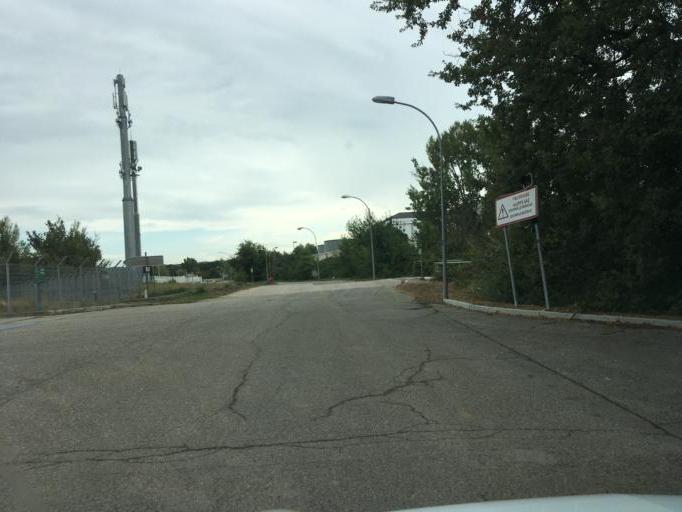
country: FR
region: Provence-Alpes-Cote d'Azur
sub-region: Departement des Bouches-du-Rhone
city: Rousset
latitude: 43.4740
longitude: 5.6014
